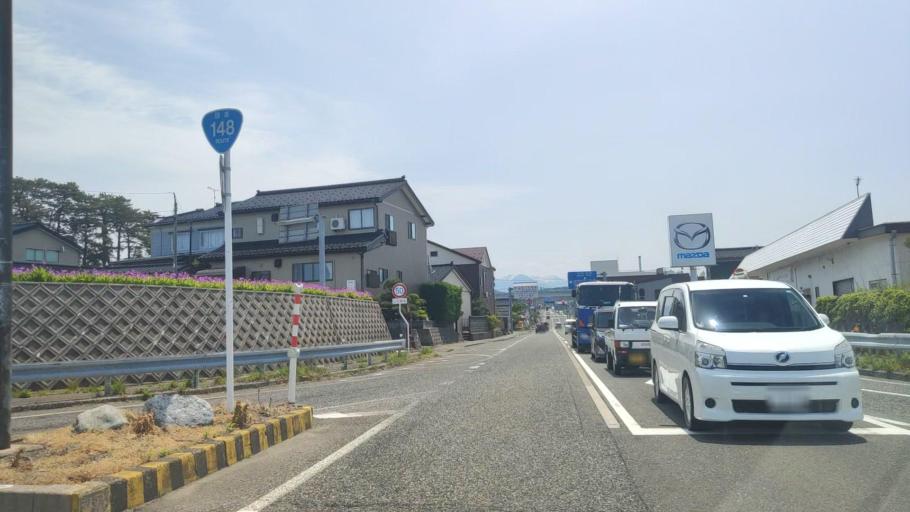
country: JP
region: Niigata
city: Itoigawa
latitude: 37.0448
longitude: 137.8504
